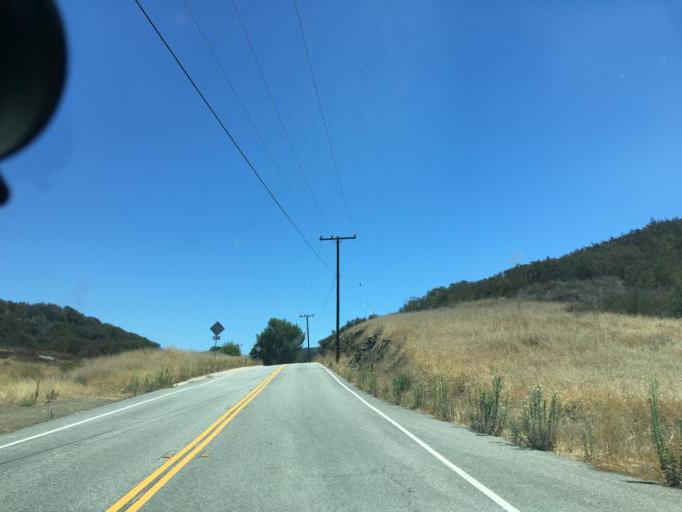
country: US
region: California
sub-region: Los Angeles County
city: Westlake Village
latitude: 34.0850
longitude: -118.8630
